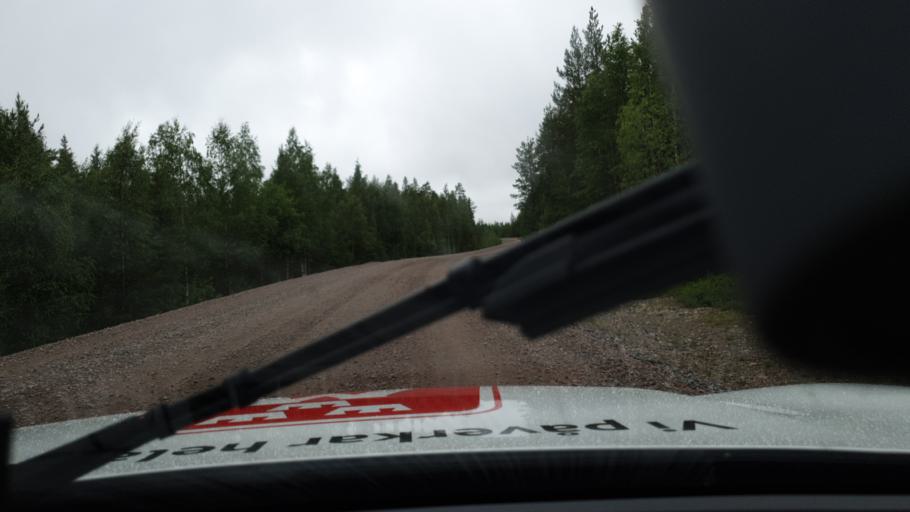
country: SE
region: Norrbotten
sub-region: Overtornea Kommun
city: OEvertornea
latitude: 66.4419
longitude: 23.4973
